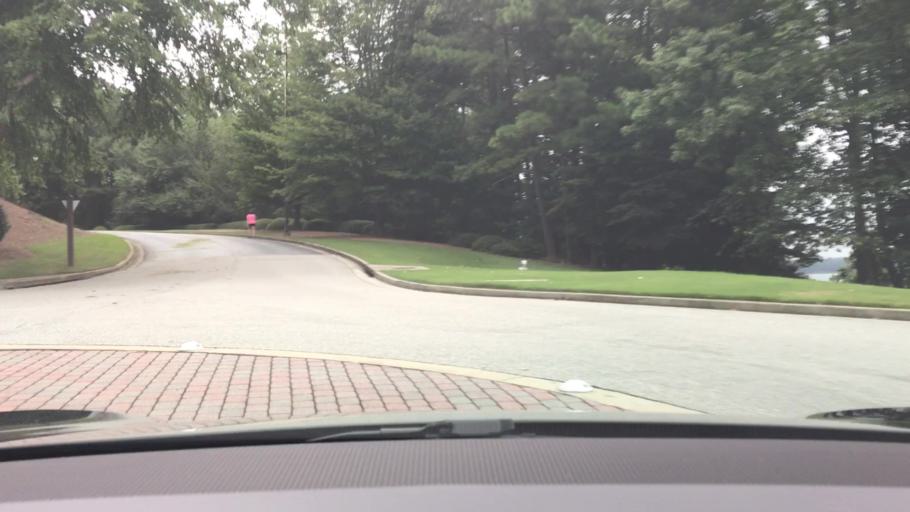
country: US
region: Georgia
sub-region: Gwinnett County
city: Buford
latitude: 34.1852
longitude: -84.0177
